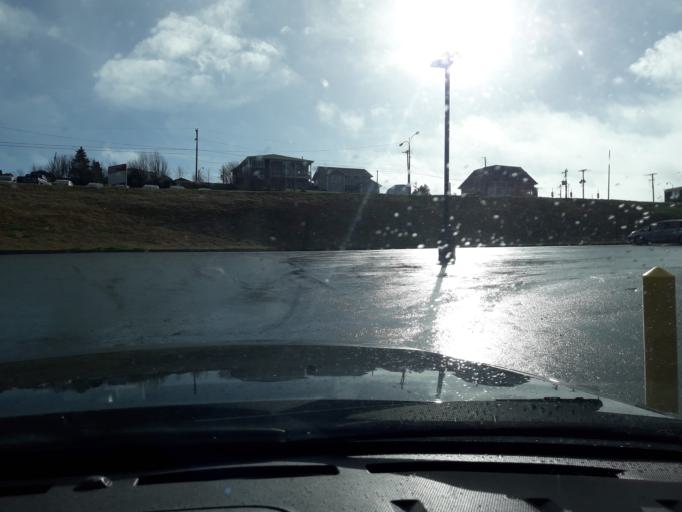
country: CA
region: Newfoundland and Labrador
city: St. John's
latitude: 47.5725
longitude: -52.6940
